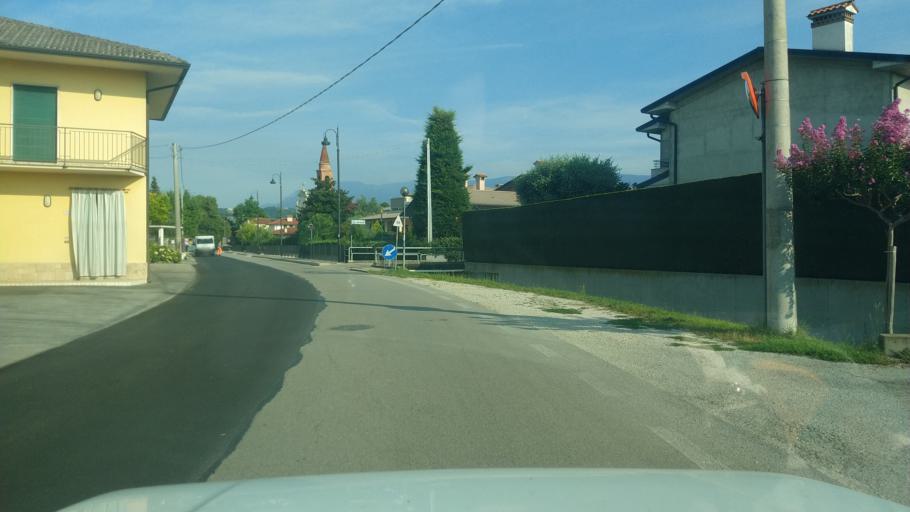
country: IT
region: Veneto
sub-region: Provincia di Vicenza
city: Mason Vicentino
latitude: 45.7167
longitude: 11.6282
